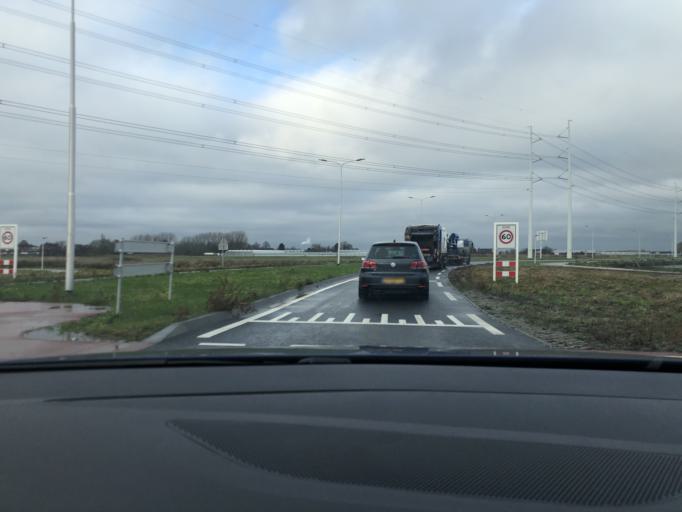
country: NL
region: South Holland
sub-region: Gemeente Lansingerland
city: Berkel en Rodenrijs
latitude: 52.0119
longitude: 4.4588
